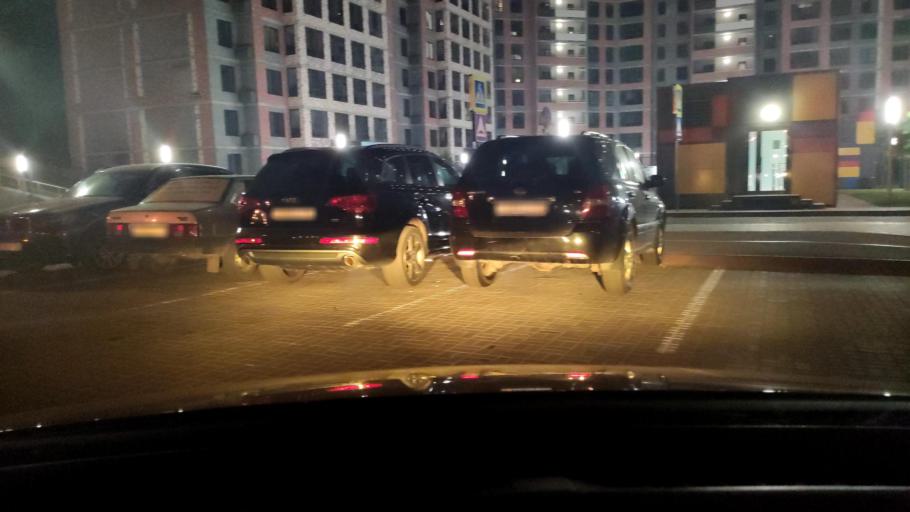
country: RU
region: Voronezj
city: Voronezh
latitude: 51.7153
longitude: 39.1997
